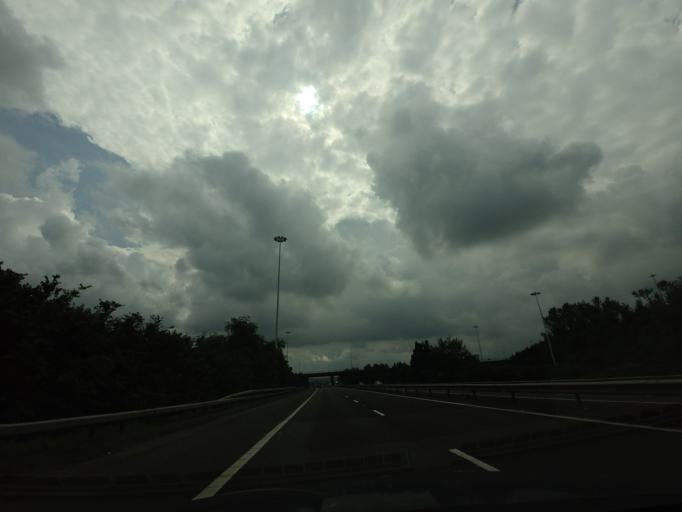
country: GB
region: Scotland
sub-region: South Lanarkshire
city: Uddingston
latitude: 55.8549
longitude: -4.0886
